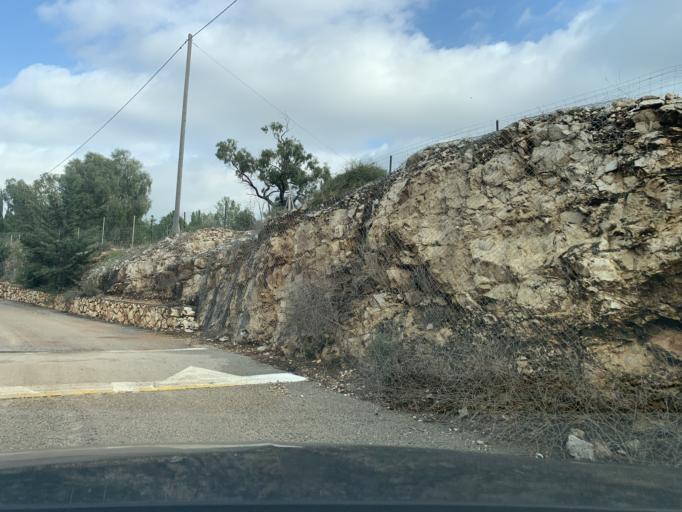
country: IL
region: Central District
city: Rosh Ha'Ayin
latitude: 32.0587
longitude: 34.9508
